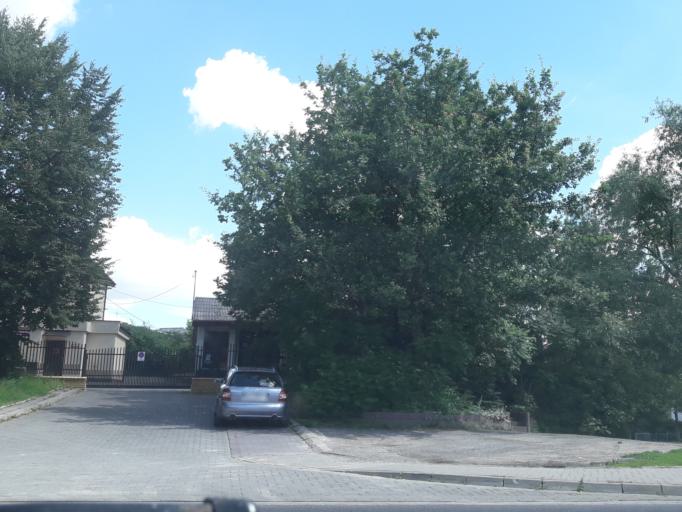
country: PL
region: Lublin Voivodeship
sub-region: Powiat lubelski
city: Lublin
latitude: 51.2535
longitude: 22.5215
